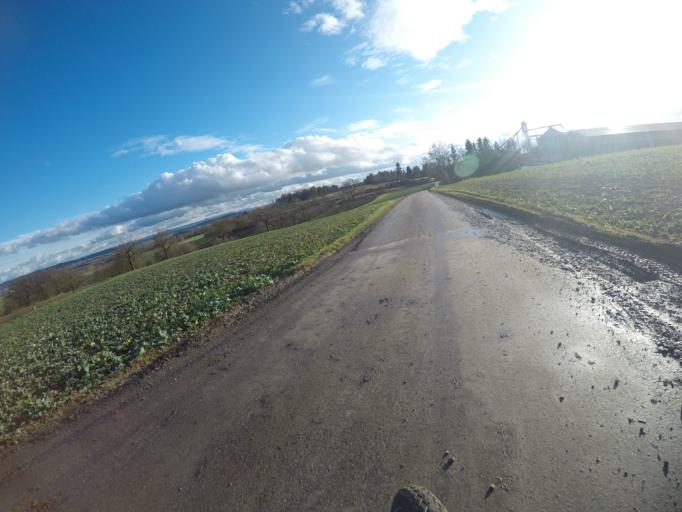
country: DE
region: Baden-Wuerttemberg
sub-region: Regierungsbezirk Stuttgart
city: Herrenberg
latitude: 48.5597
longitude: 8.8668
